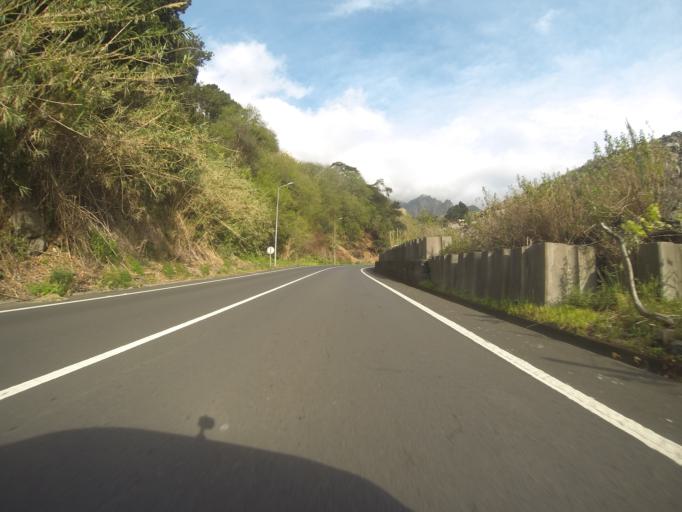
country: PT
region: Madeira
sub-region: Sao Vicente
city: Sao Vicente
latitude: 32.7896
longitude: -17.0301
